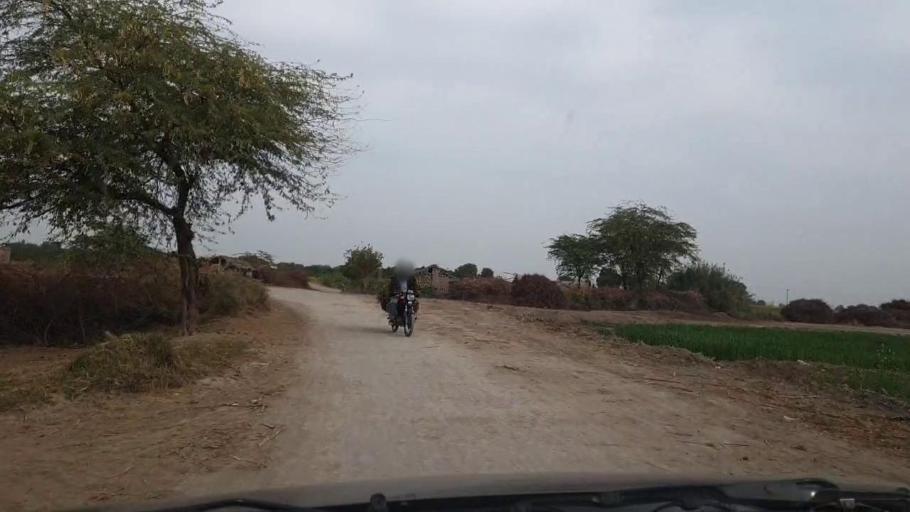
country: PK
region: Sindh
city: Sanghar
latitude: 26.0975
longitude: 68.9000
